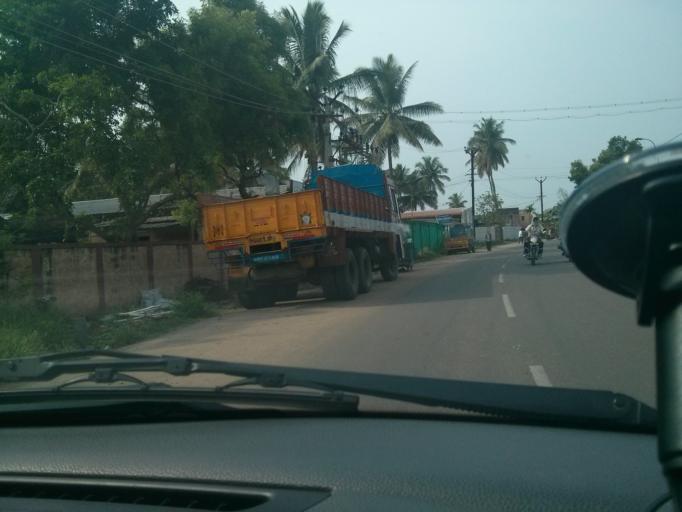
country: IN
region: Tamil Nadu
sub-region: Coimbatore
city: Coimbatore
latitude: 11.0364
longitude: 76.9616
